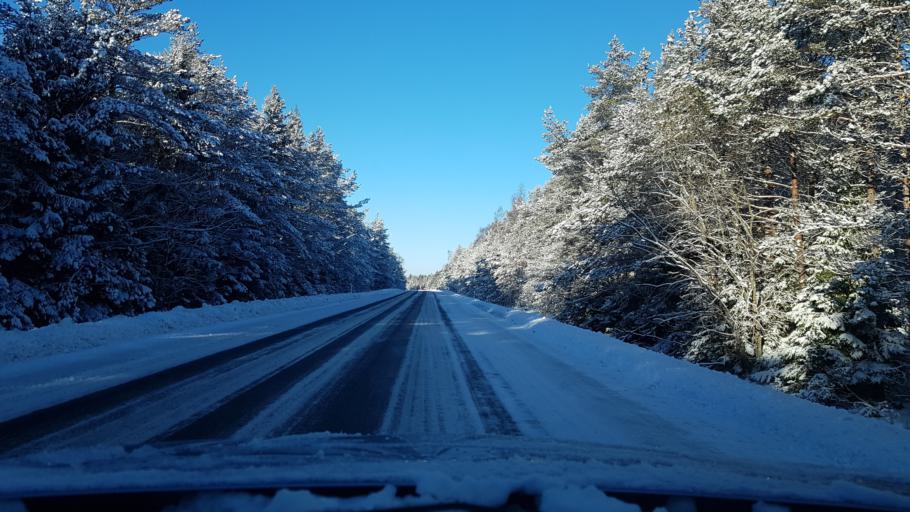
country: EE
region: Hiiumaa
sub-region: Kaerdla linn
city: Kardla
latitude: 58.9860
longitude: 22.7975
